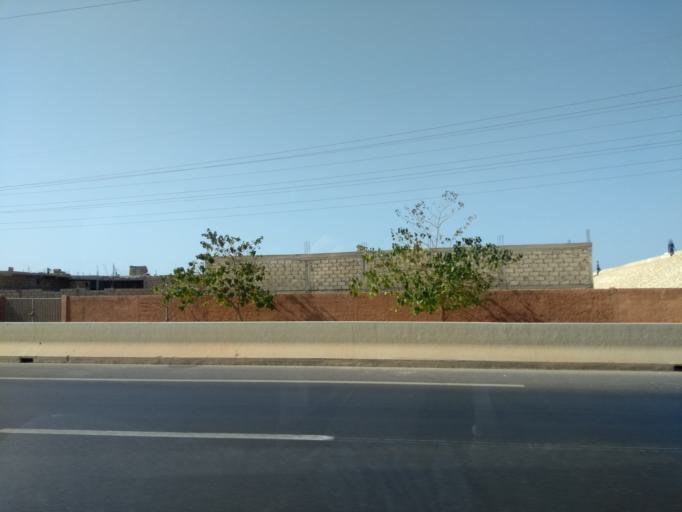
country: SN
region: Dakar
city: Pikine
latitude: 14.7474
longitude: -17.3852
